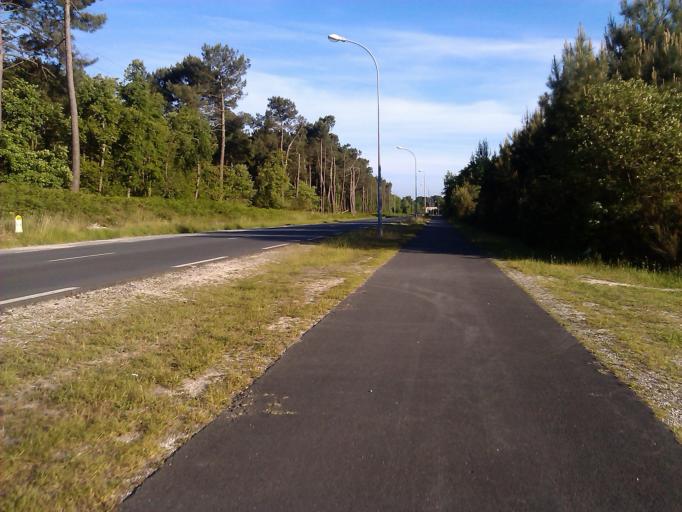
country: FR
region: Aquitaine
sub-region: Departement de la Gironde
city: Cestas
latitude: 44.7665
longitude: -0.6906
